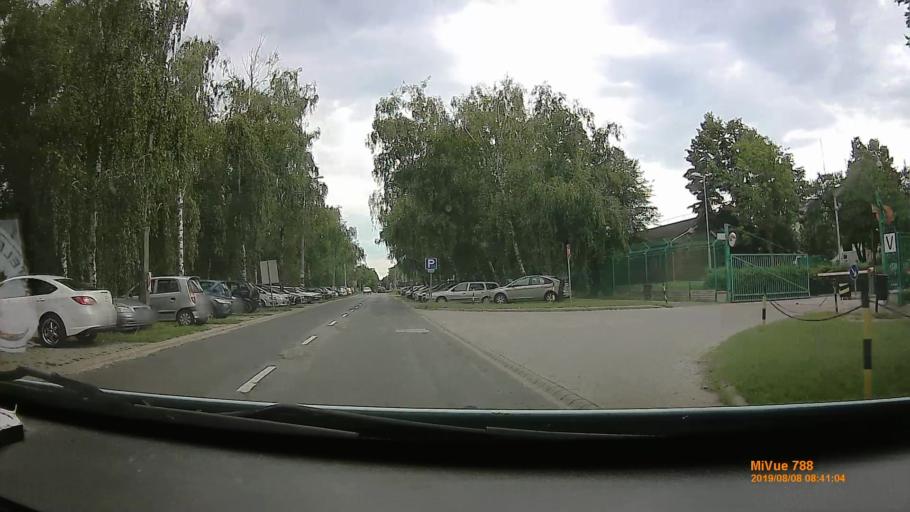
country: HU
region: Hajdu-Bihar
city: Debrecen
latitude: 47.5620
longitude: 21.6305
